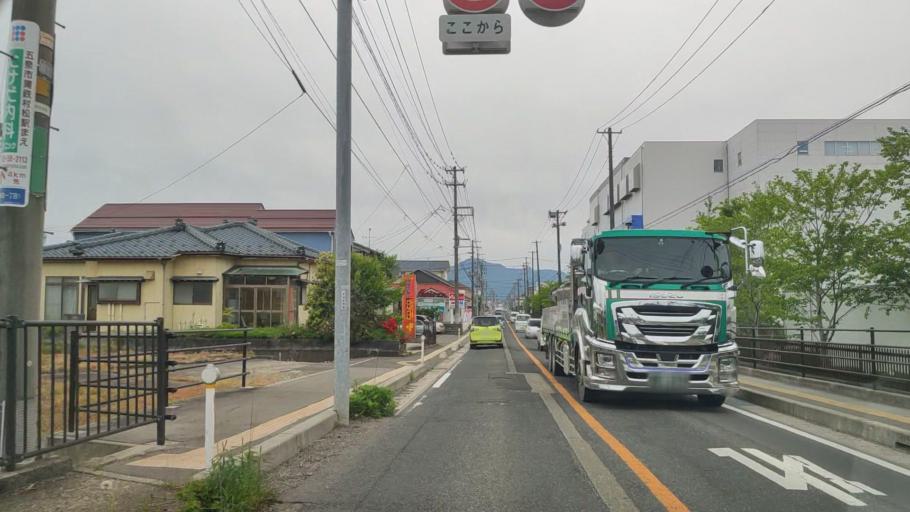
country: JP
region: Niigata
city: Gosen
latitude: 37.7354
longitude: 139.1765
